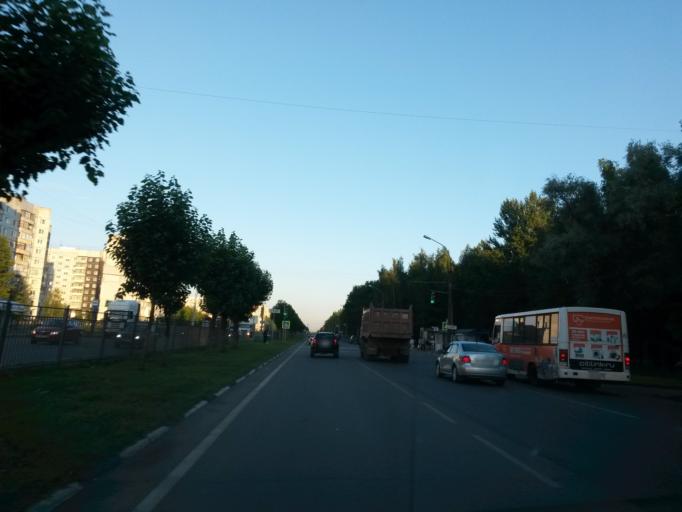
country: RU
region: Jaroslavl
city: Yaroslavl
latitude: 57.6928
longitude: 39.7725
